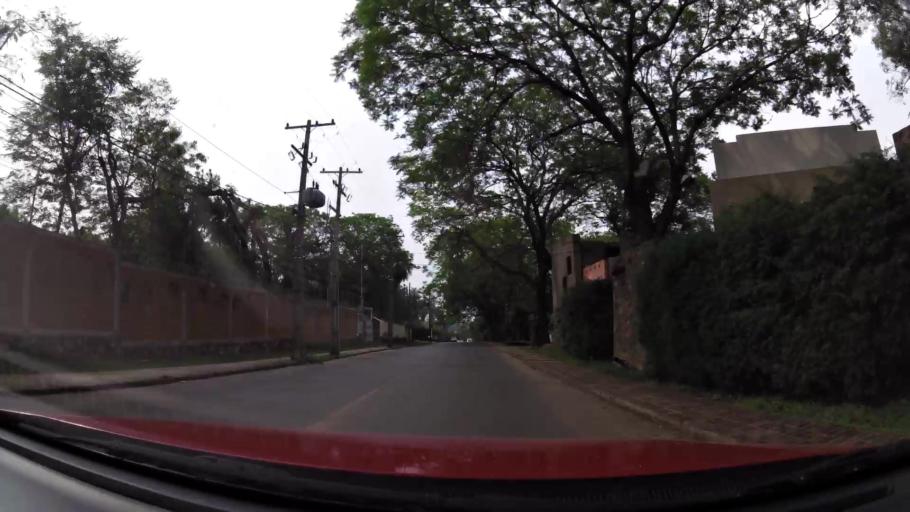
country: PY
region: Central
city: Fernando de la Mora
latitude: -25.2827
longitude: -57.5530
